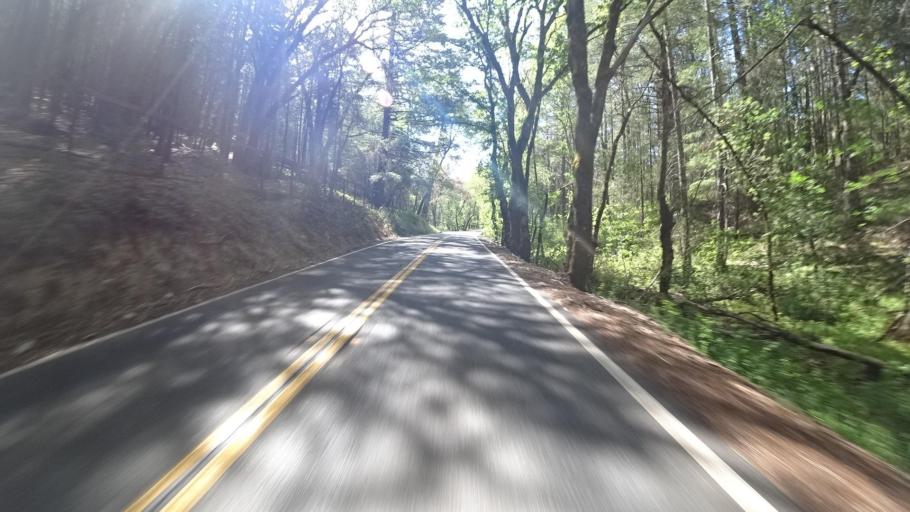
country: US
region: California
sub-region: Lake County
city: Cobb
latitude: 38.8937
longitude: -122.7362
